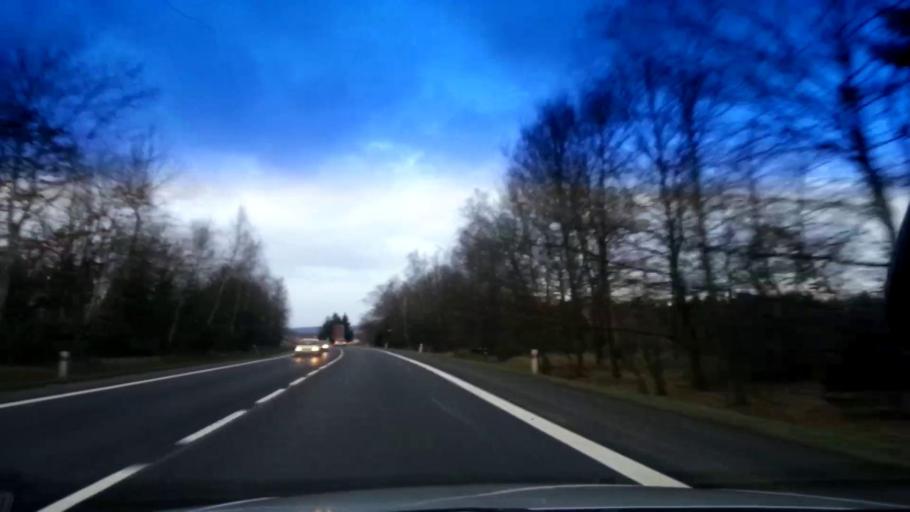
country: CZ
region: Karlovarsky
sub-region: Okres Cheb
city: Frantiskovy Lazne
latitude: 50.1203
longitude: 12.3707
